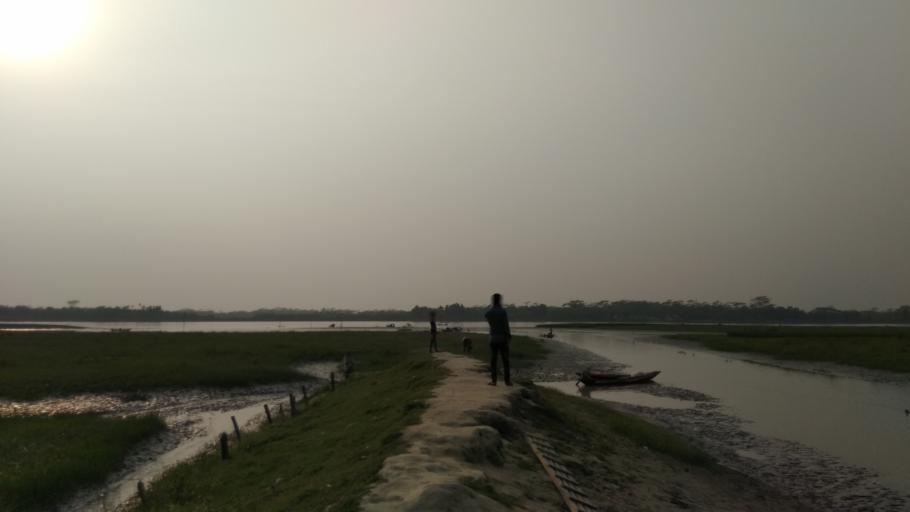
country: BD
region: Barisal
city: Mehendiganj
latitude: 22.9106
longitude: 90.3969
